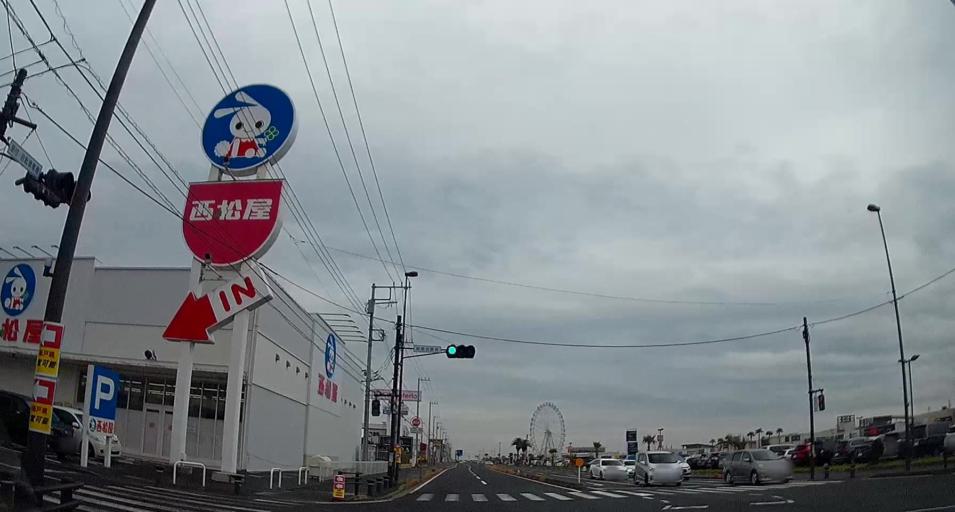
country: JP
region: Chiba
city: Kisarazu
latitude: 35.4338
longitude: 139.9324
